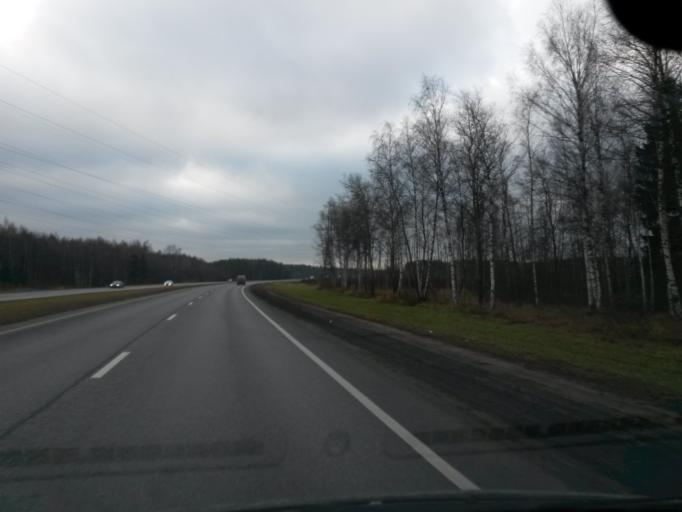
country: RU
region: Jaroslavl
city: Krasnyye Tkachi
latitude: 57.4941
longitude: 39.7834
